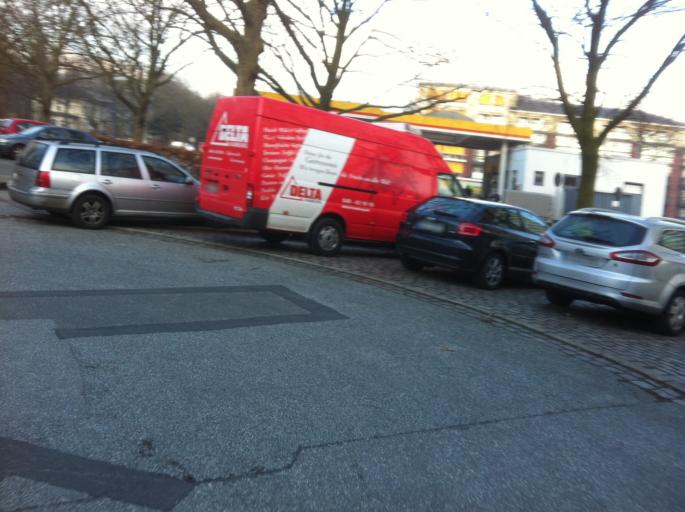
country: DE
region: Hamburg
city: St. Pauli
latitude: 53.5684
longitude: 9.9508
